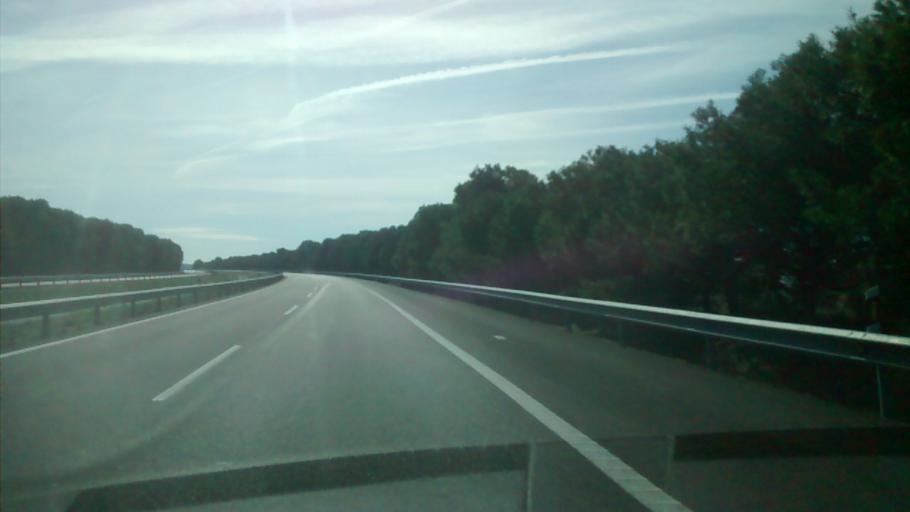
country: ES
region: Aragon
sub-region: Provincia de Zaragoza
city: Pina de Ebro
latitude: 41.5259
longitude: -0.5021
